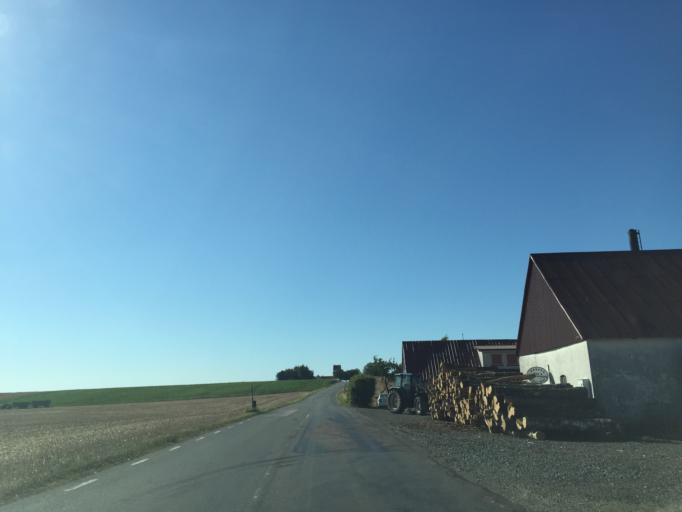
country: SE
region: Skane
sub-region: Ystads Kommun
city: Kopingebro
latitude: 55.4494
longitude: 14.1193
